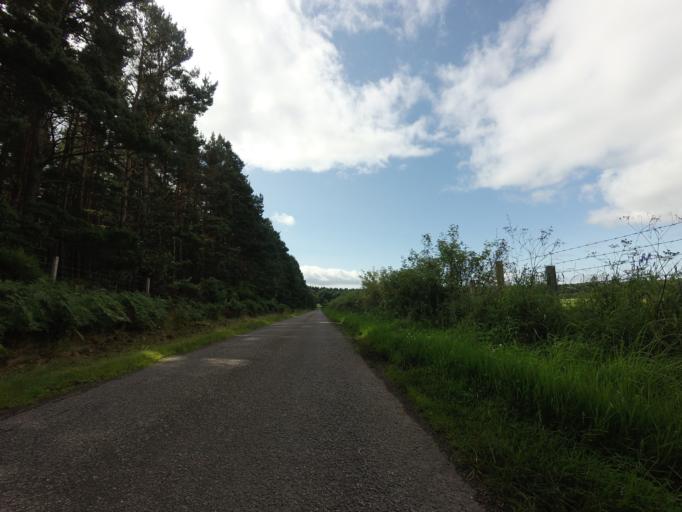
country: GB
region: Scotland
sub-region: Highland
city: Nairn
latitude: 57.5636
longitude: -3.8670
